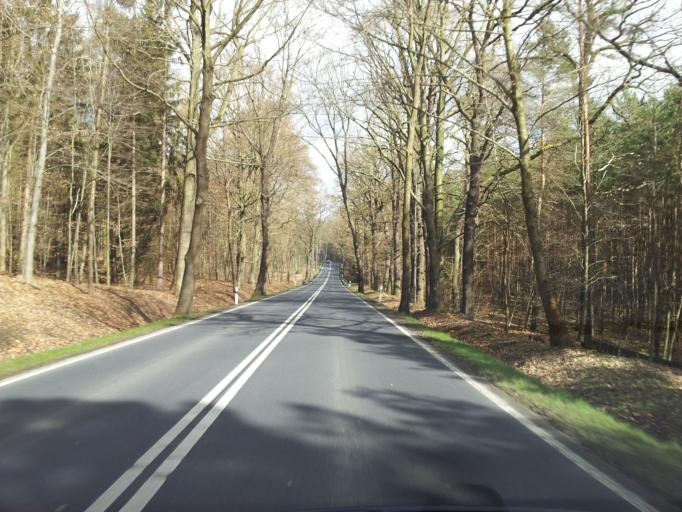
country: DE
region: Saxony
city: Ottendorf-Okrilla
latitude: 51.2248
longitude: 13.8439
